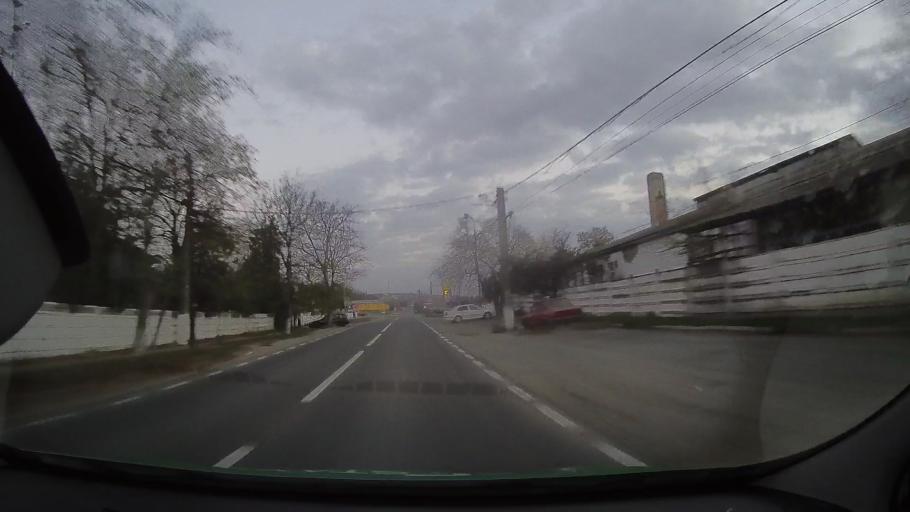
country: RO
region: Constanta
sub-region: Comuna Baneasa
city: Baneasa
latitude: 44.0693
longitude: 27.6926
